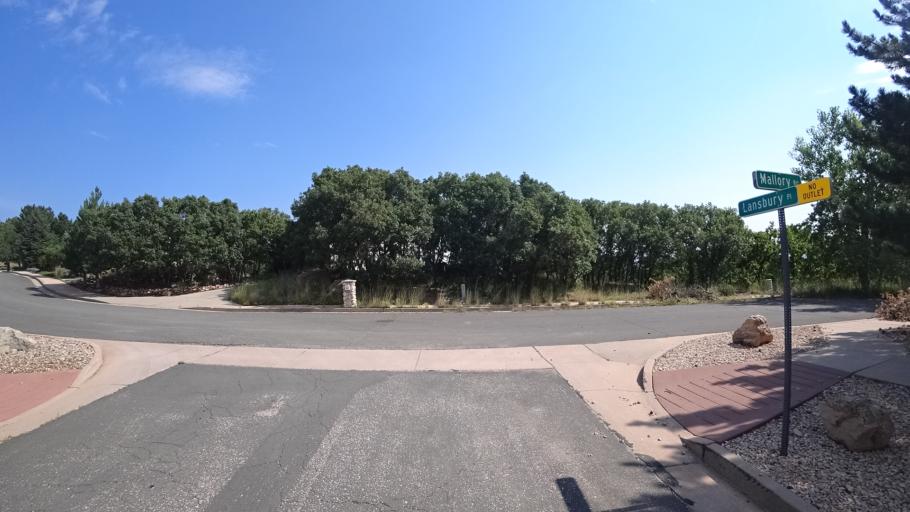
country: US
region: Colorado
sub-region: El Paso County
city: Fort Carson
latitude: 38.7541
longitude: -104.8317
